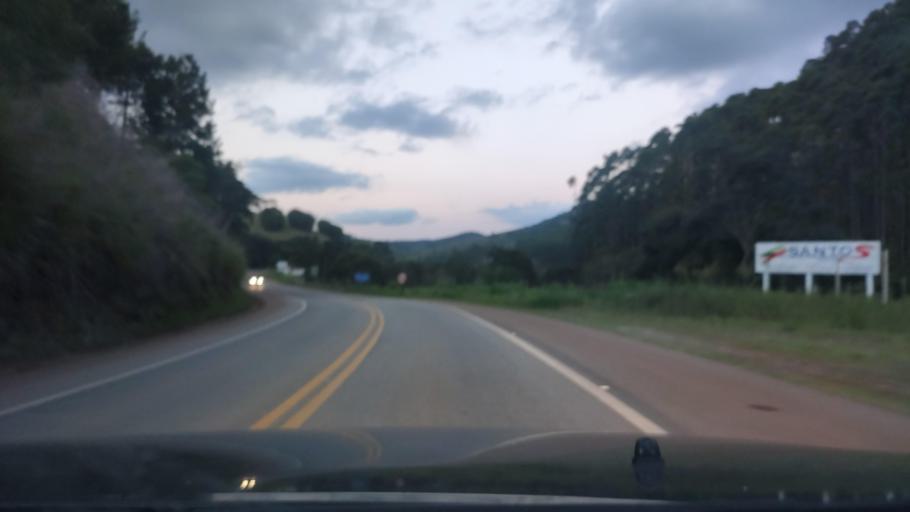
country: BR
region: Sao Paulo
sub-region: Campos Do Jordao
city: Campos do Jordao
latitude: -22.7950
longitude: -45.7461
